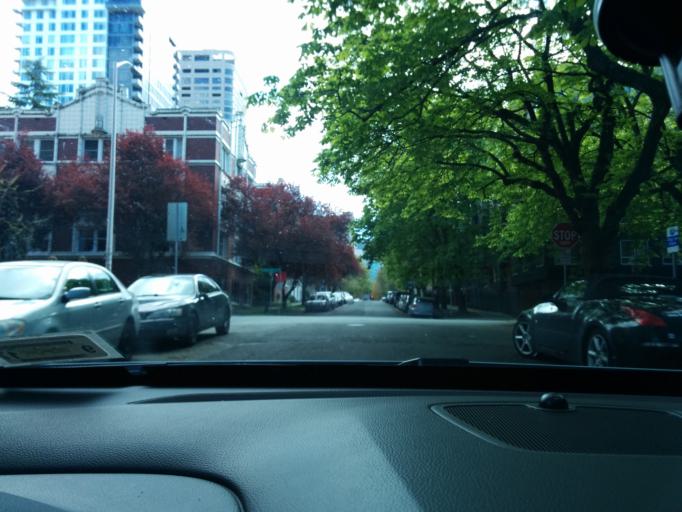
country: US
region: Washington
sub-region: King County
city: Seattle
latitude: 47.6127
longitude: -122.3252
